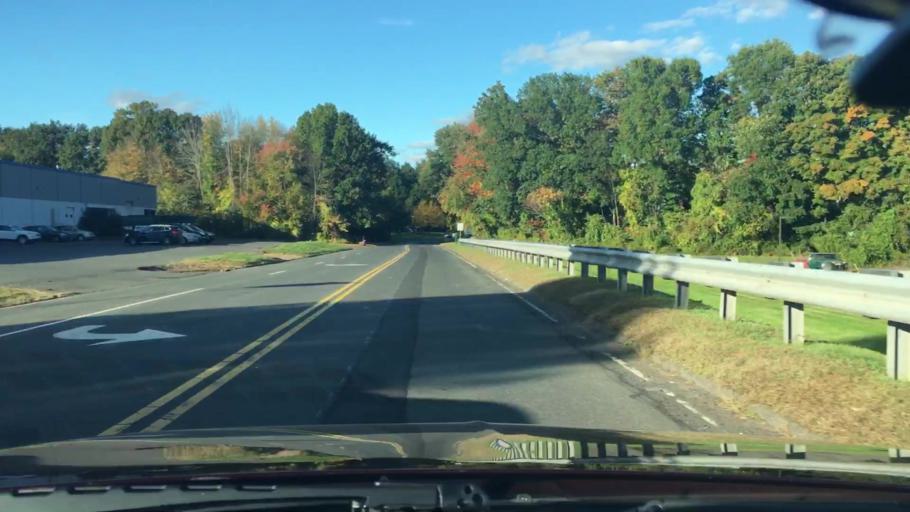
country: US
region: Connecticut
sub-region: Hartford County
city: Windsor
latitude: 41.8565
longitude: -72.6788
